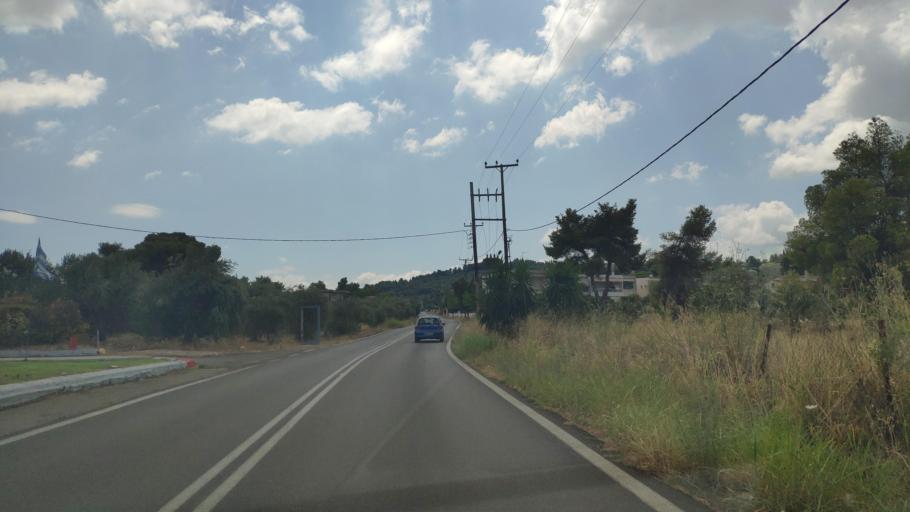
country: GR
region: Central Greece
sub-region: Nomos Fthiotidos
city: Malesina
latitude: 38.6504
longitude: 23.1973
